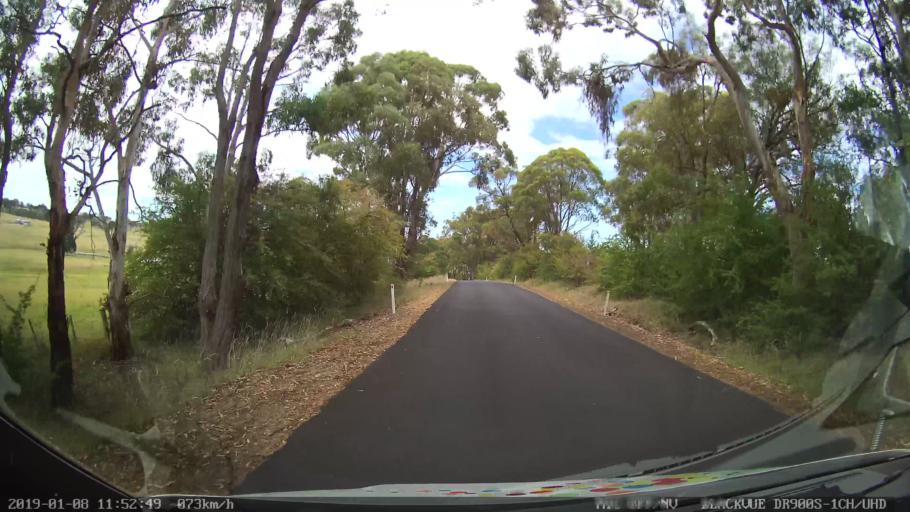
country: AU
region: New South Wales
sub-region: Armidale Dumaresq
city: Armidale
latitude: -30.4073
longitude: 151.5598
